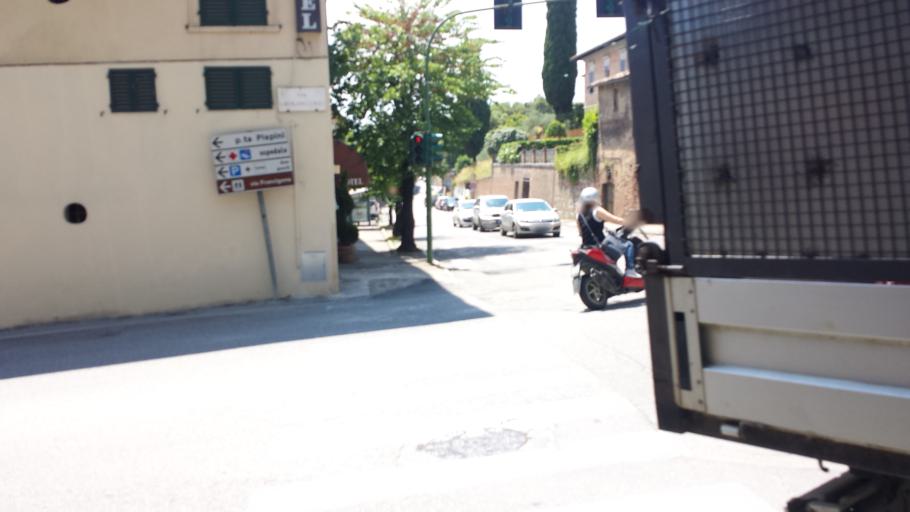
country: IT
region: Tuscany
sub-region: Provincia di Siena
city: Siena
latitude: 43.3118
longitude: 11.3393
